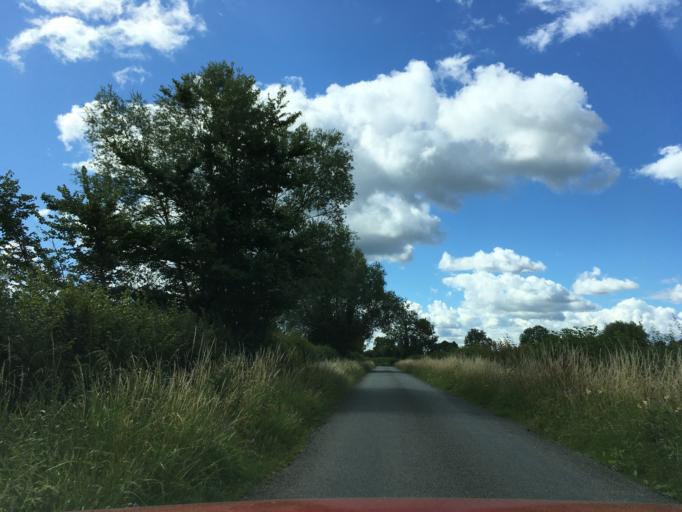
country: GB
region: England
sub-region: Gloucestershire
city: Newent
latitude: 51.8513
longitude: -2.3520
